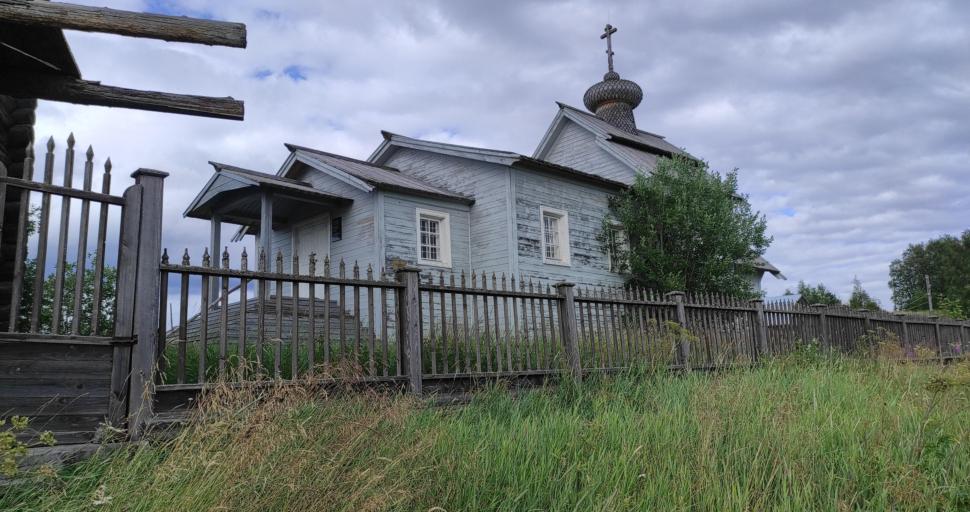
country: RU
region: Murmansk
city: Poyakonda
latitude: 66.6922
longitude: 32.8609
